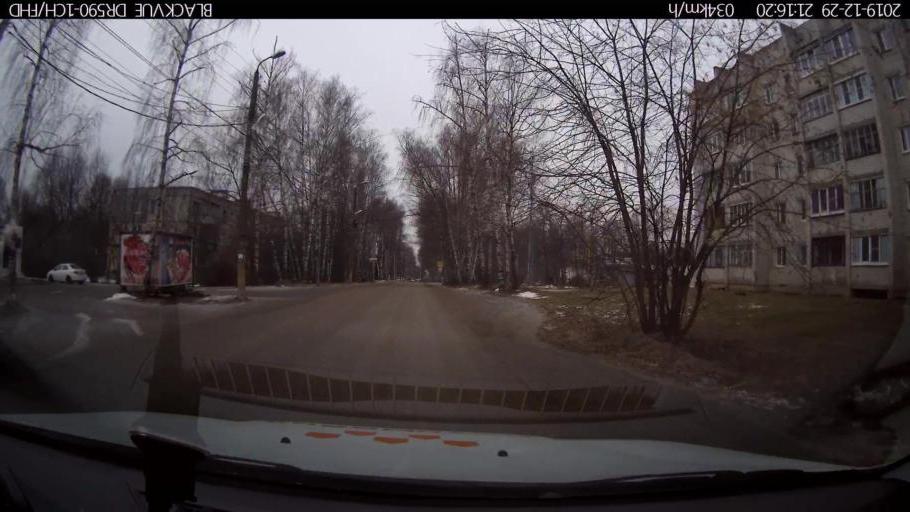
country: RU
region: Nizjnij Novgorod
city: Afonino
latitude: 56.2104
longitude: 44.0229
